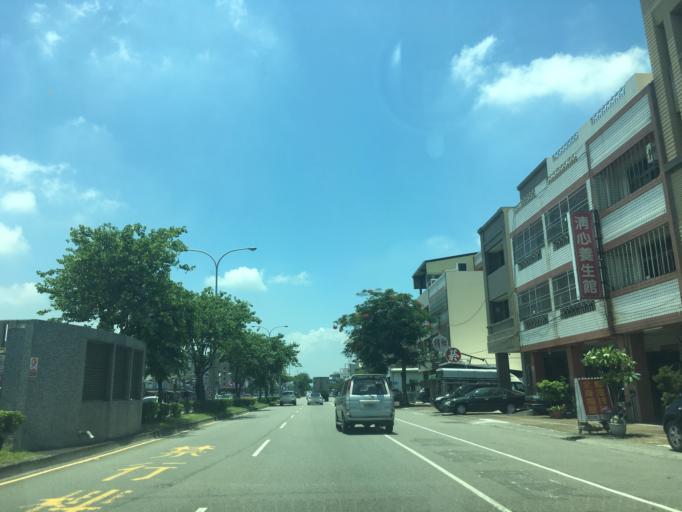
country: TW
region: Taiwan
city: Fengyuan
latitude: 24.2464
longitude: 120.7032
